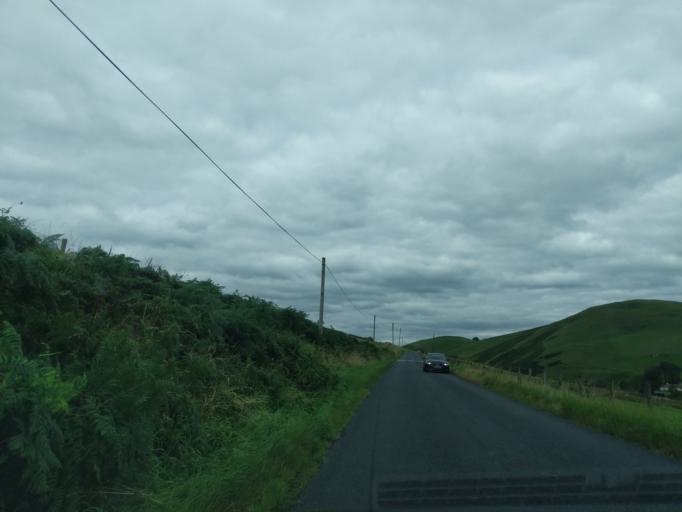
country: GB
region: Scotland
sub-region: The Scottish Borders
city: West Linton
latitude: 55.6881
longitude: -3.3339
